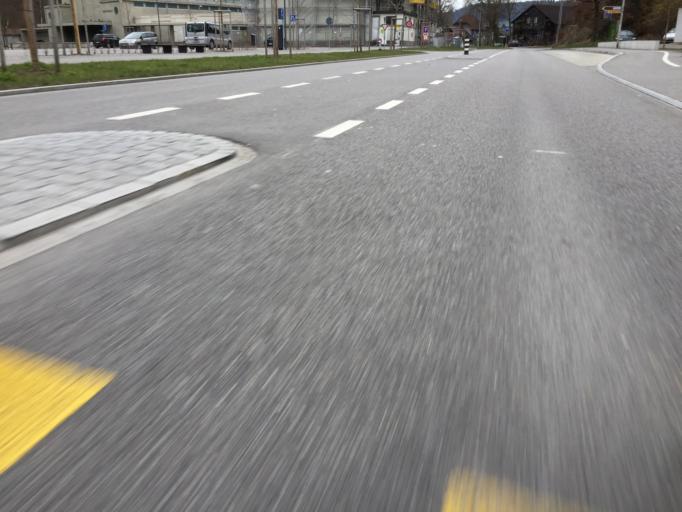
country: CH
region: Bern
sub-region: Emmental District
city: Burgdorf
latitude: 47.0560
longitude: 7.6304
